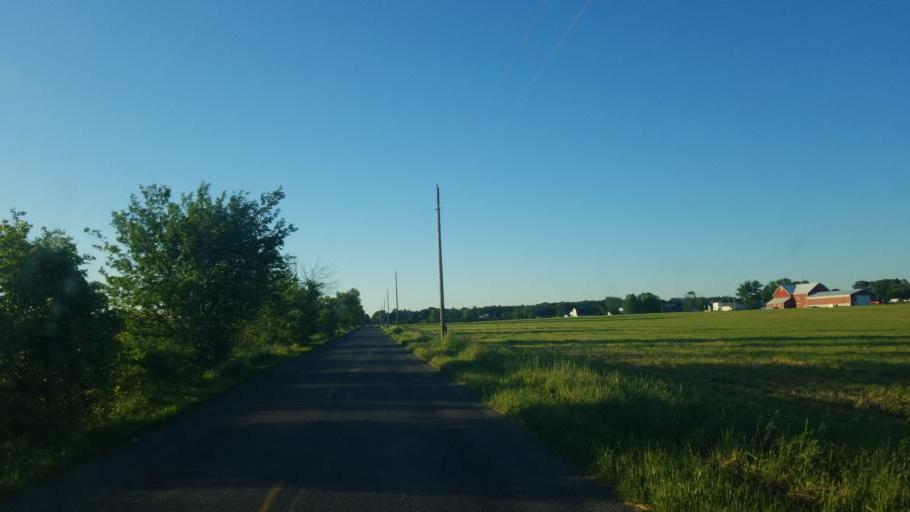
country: US
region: Indiana
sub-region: Elkhart County
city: Nappanee
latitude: 41.4387
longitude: -86.0496
